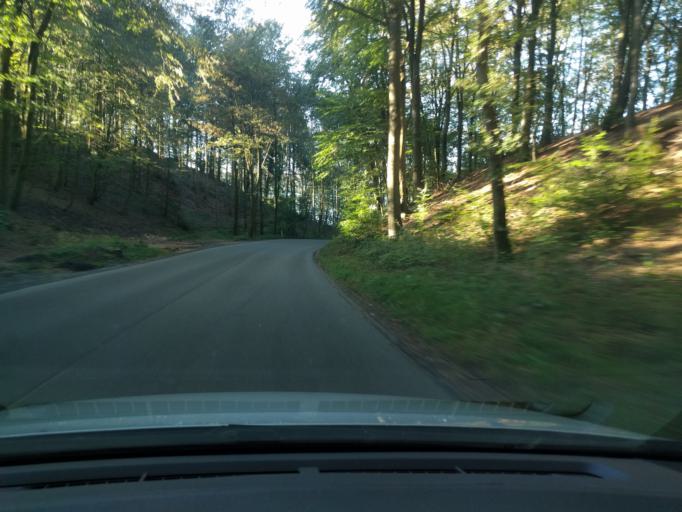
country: DK
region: Central Jutland
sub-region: Skanderborg Kommune
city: Ry
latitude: 56.0957
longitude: 9.7811
